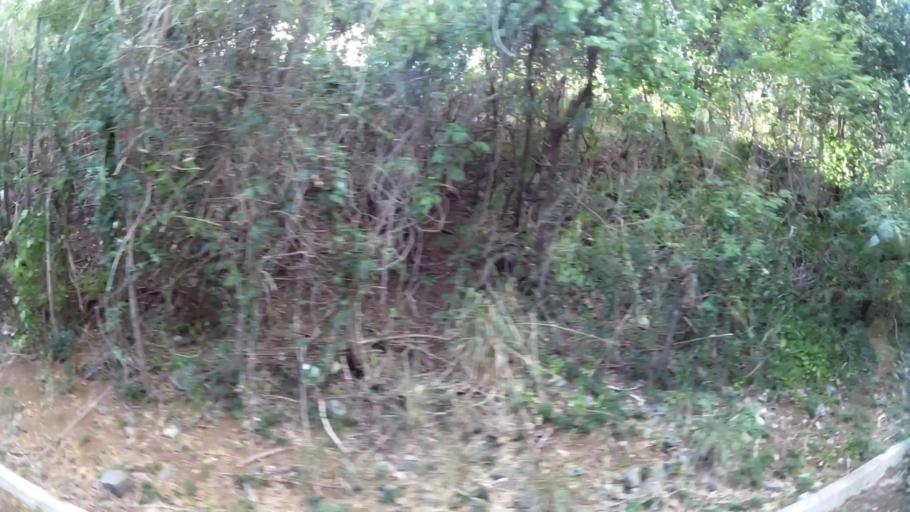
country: VG
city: Road Town
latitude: 18.3941
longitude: -64.6779
